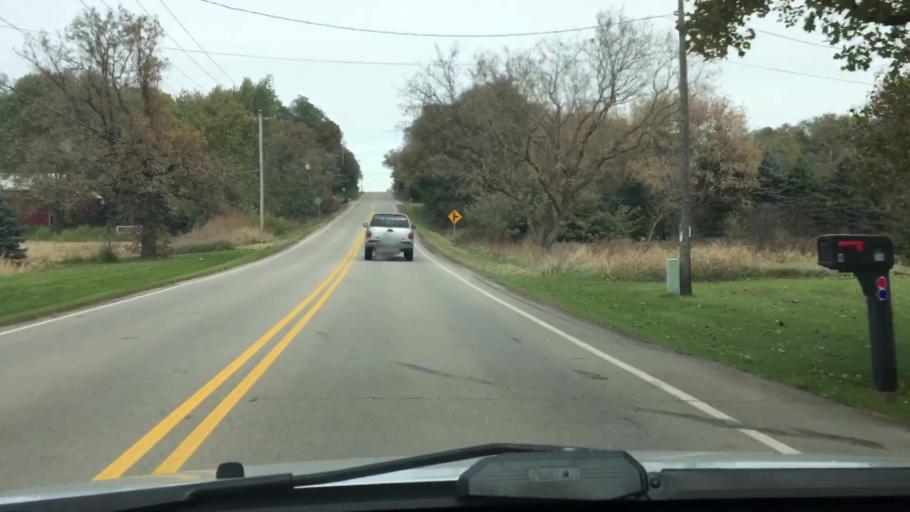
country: US
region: Wisconsin
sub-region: Waukesha County
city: North Prairie
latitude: 42.9208
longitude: -88.4054
